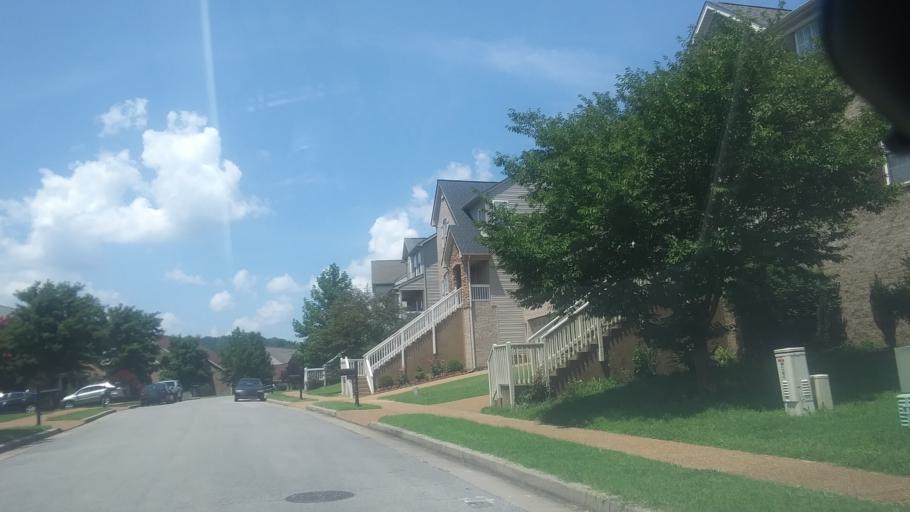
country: US
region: Tennessee
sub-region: Davidson County
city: Belle Meade
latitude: 36.1190
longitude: -86.9325
